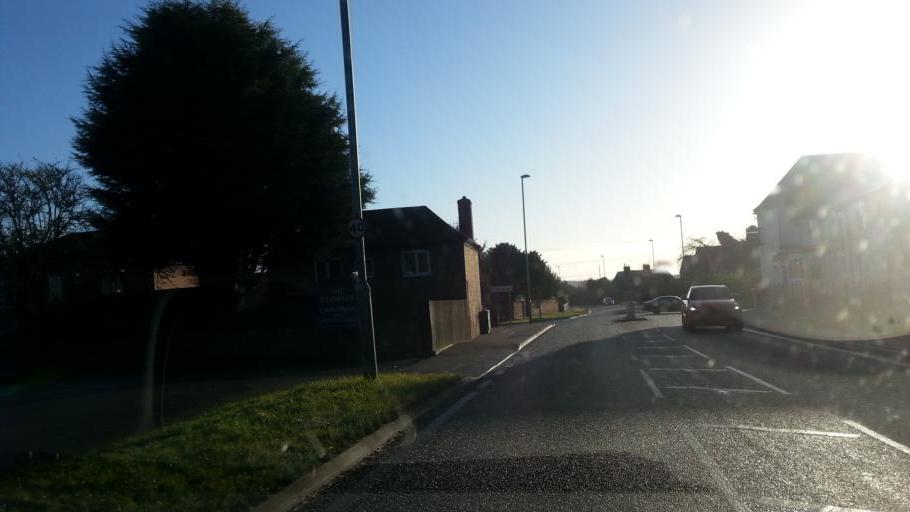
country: GB
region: England
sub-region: Nottinghamshire
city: South Collingham
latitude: 53.0817
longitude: -0.7541
